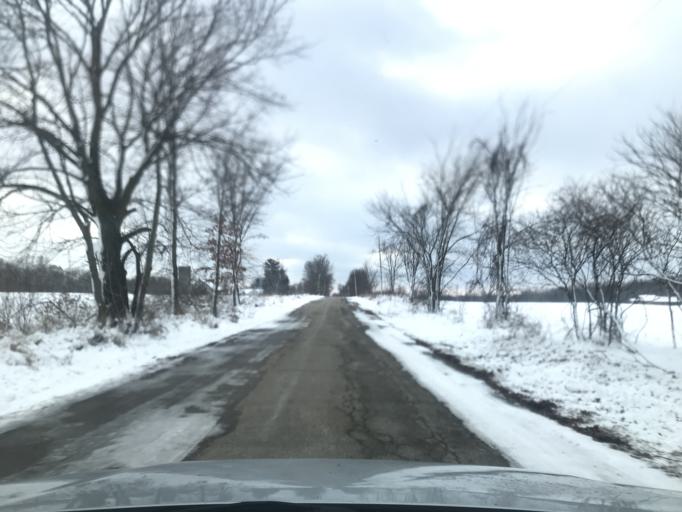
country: US
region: Wisconsin
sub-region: Oconto County
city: Oconto
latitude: 44.9225
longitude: -87.9988
